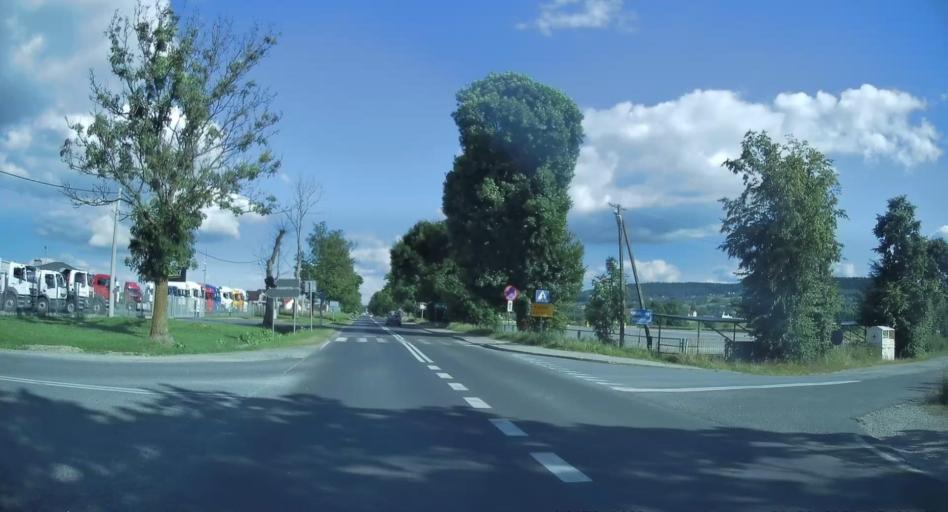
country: PL
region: Swietokrzyskie
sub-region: Powiat kielecki
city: Bodzentyn
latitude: 50.9502
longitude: 20.9282
